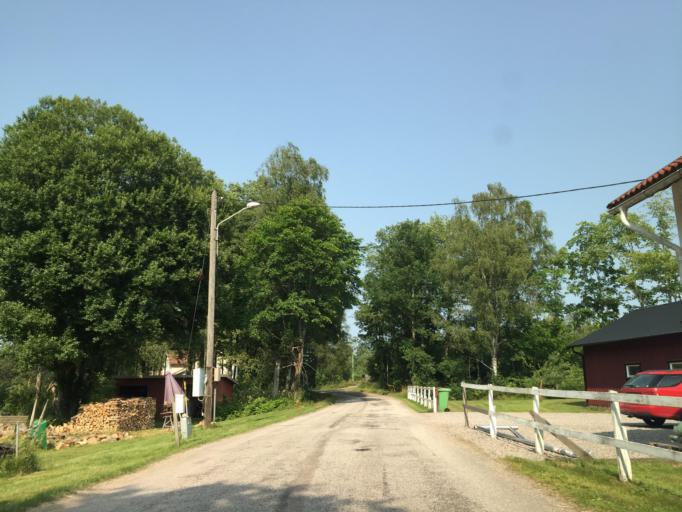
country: SE
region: Vaestra Goetaland
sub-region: Vanersborgs Kommun
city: Vanersborg
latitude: 58.3599
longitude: 12.2733
